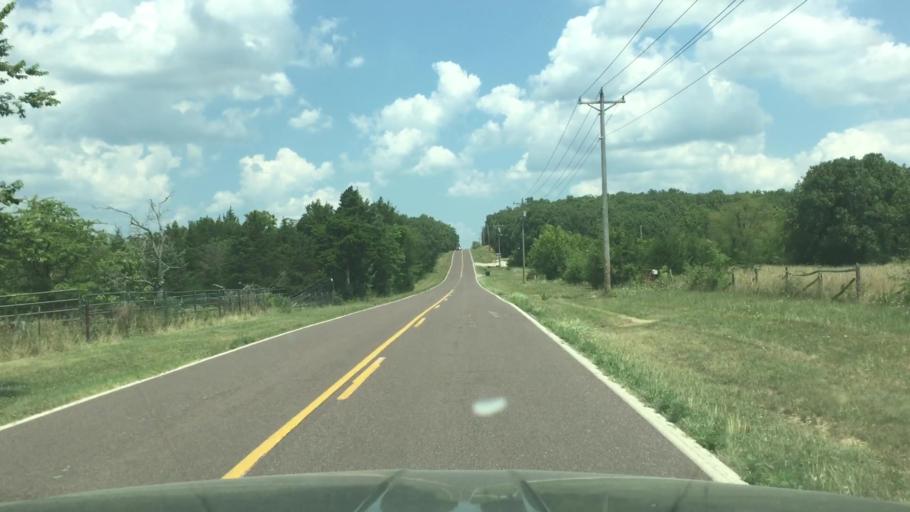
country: US
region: Missouri
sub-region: Miller County
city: Tuscumbia
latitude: 38.1096
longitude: -92.4730
